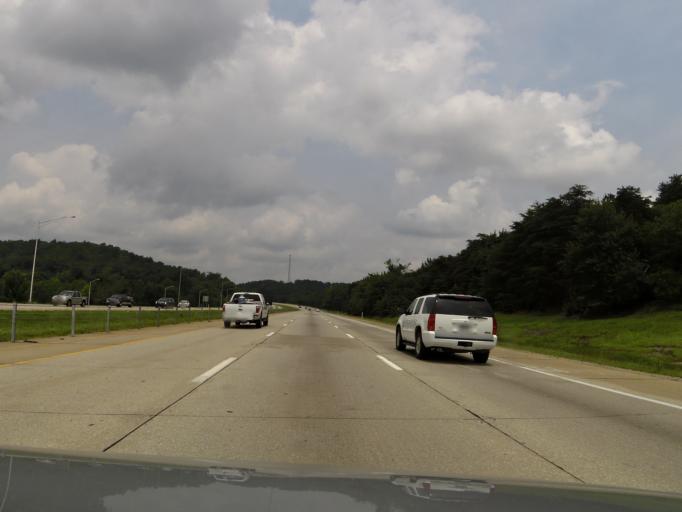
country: US
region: Kentucky
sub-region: Bullitt County
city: Shepherdsville
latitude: 37.9481
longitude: -85.6888
